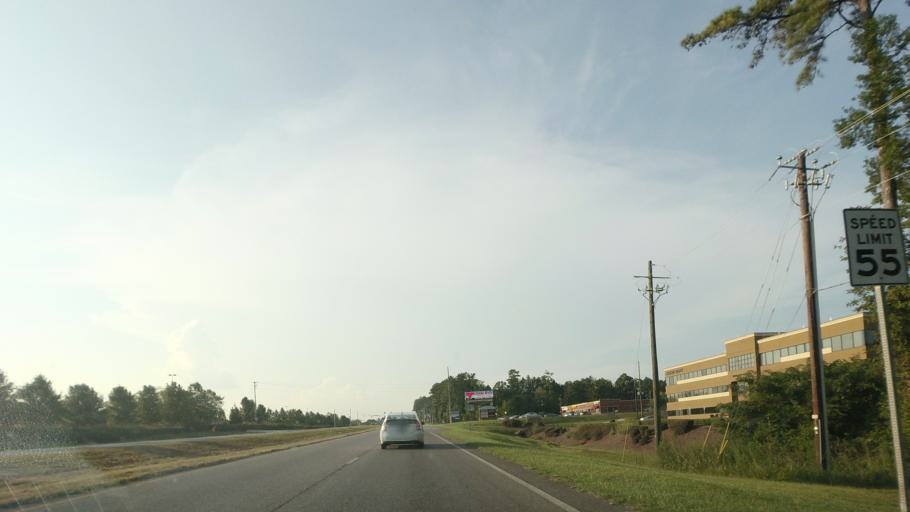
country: US
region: Georgia
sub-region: Bibb County
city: Macon
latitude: 32.9249
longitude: -83.7116
